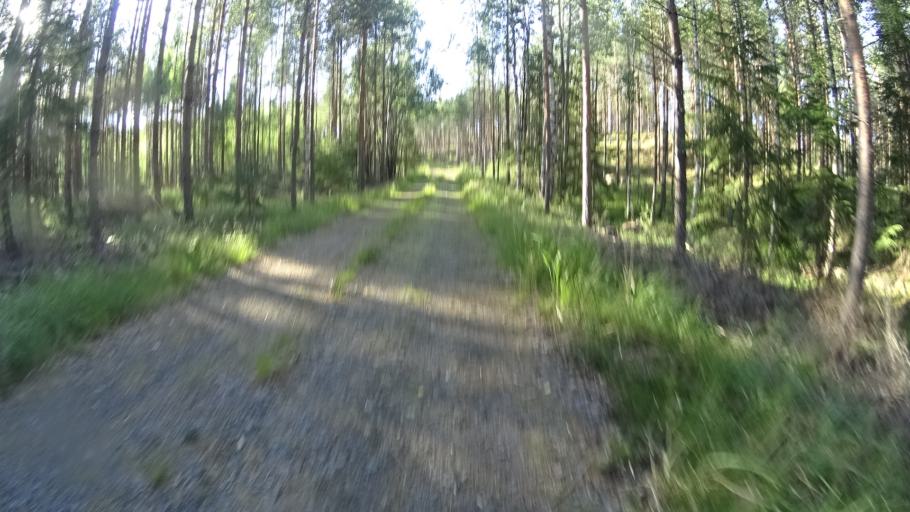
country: FI
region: Uusimaa
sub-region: Helsinki
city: Karkkila
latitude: 60.6636
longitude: 24.1326
